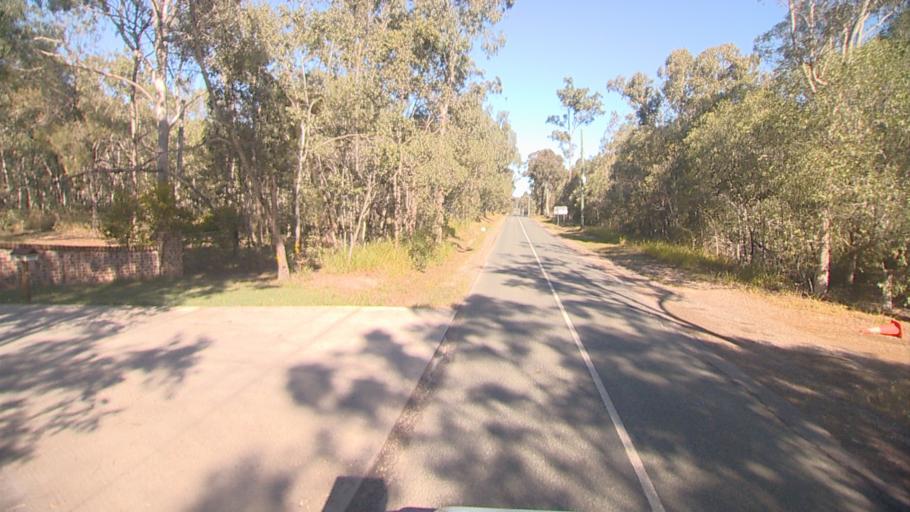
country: AU
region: Queensland
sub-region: Logan
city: Chambers Flat
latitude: -27.7938
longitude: 153.0702
